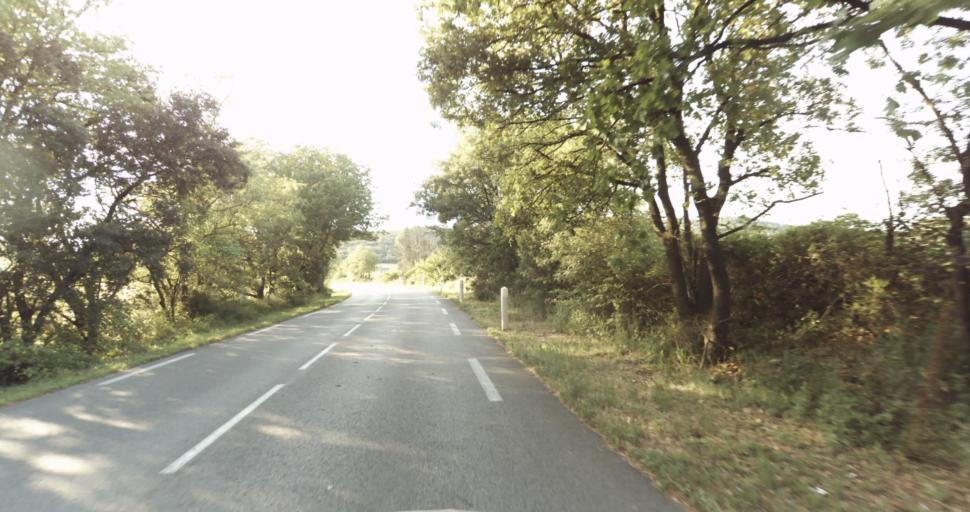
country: FR
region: Provence-Alpes-Cote d'Azur
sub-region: Departement du Var
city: Hyeres
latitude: 43.1502
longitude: 6.1476
